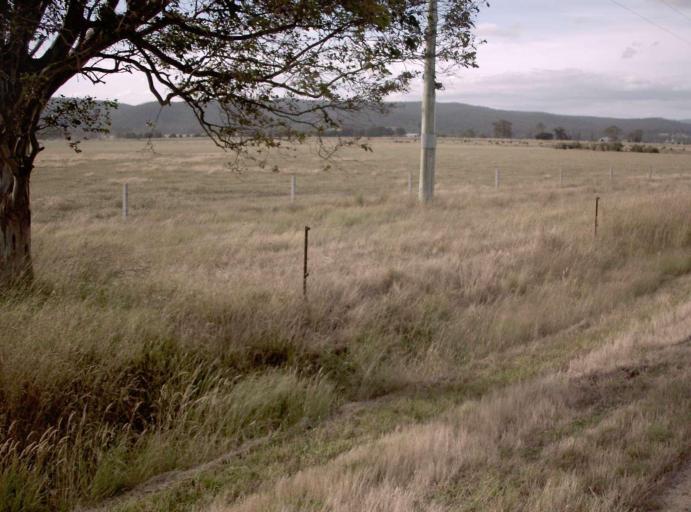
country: AU
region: Victoria
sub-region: Wellington
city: Heyfield
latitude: -38.0179
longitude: 146.6705
